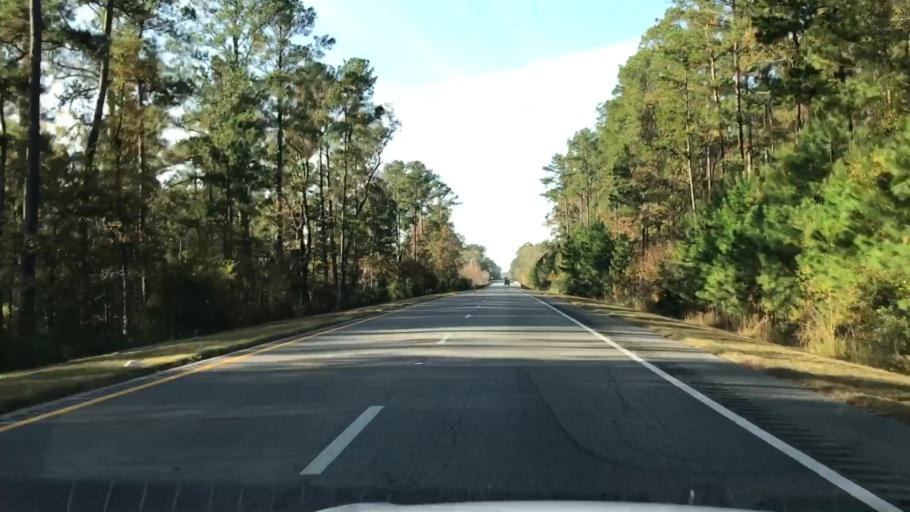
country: US
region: South Carolina
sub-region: Hampton County
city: Yemassee
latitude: 32.6413
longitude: -80.7108
